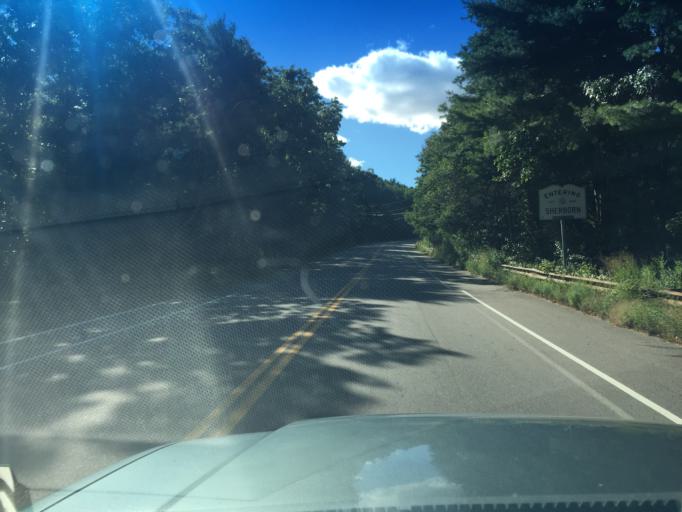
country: US
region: Massachusetts
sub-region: Middlesex County
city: Sherborn
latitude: 42.2100
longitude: -71.3519
